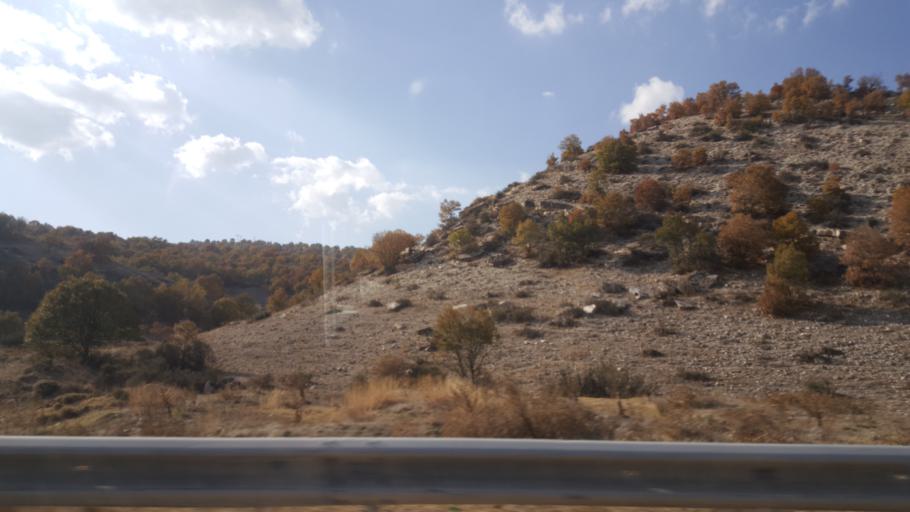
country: TR
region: Eskisehir
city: Kirka
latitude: 39.3418
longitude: 30.5786
